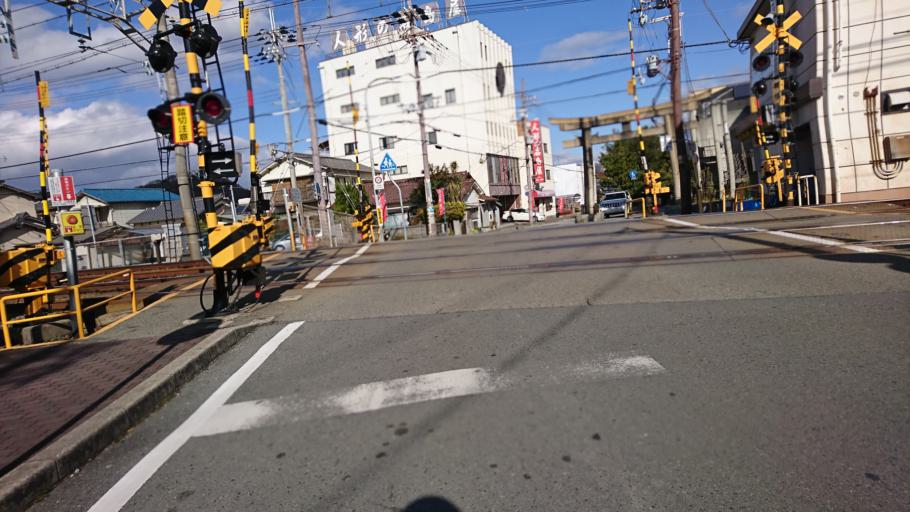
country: JP
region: Hyogo
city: Shirahamacho-usazakiminami
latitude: 34.7754
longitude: 134.7726
